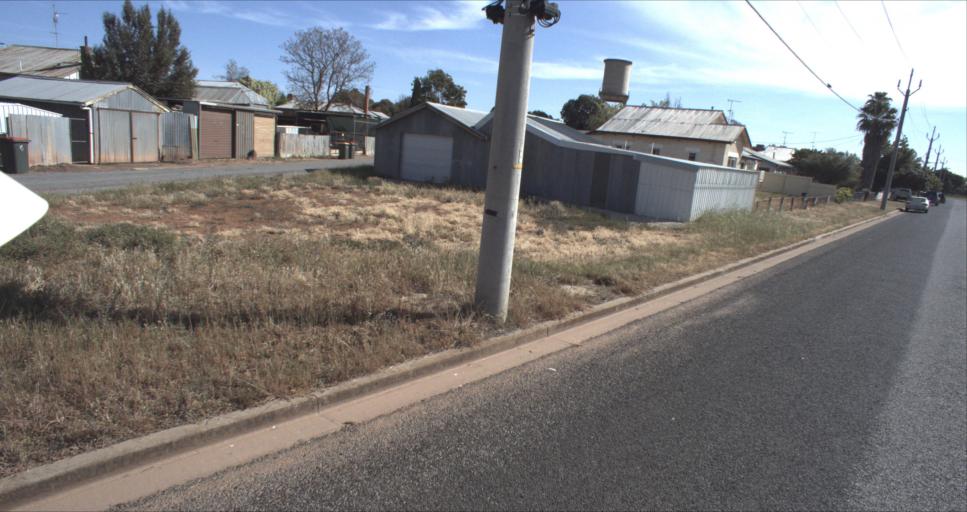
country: AU
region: New South Wales
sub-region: Leeton
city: Leeton
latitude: -34.6041
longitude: 146.4107
